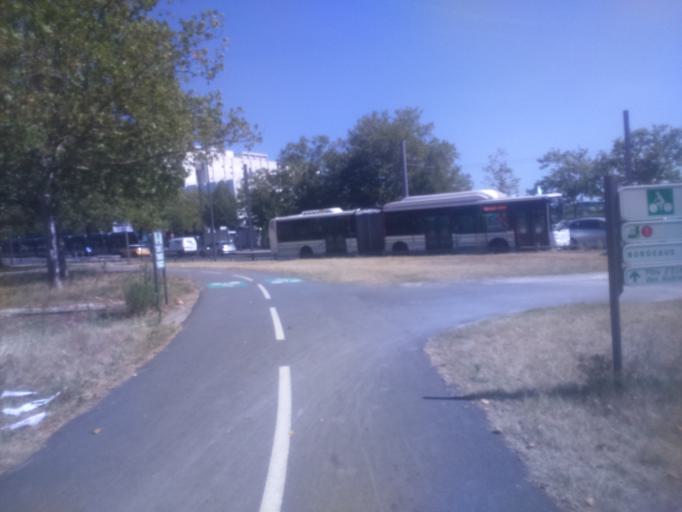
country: FR
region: Aquitaine
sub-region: Departement de la Gironde
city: Le Bouscat
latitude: 44.8743
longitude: -0.5761
